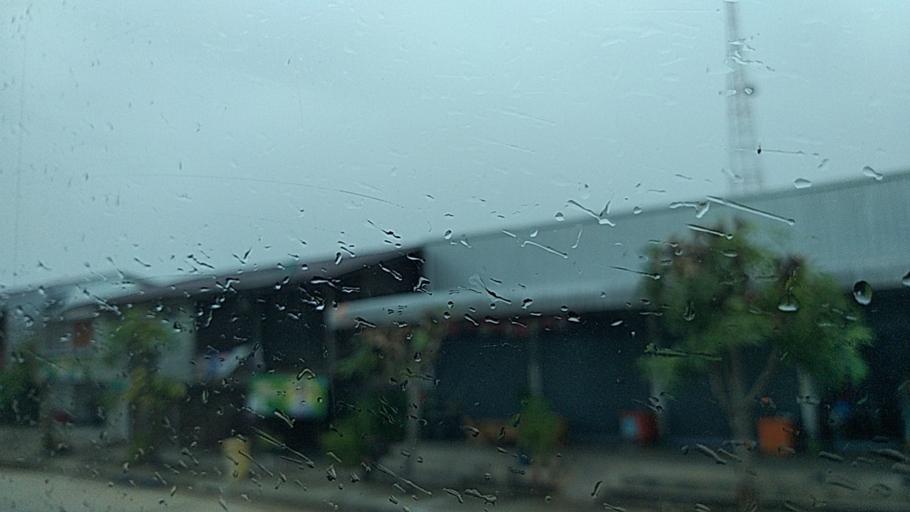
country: TH
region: Maha Sarakham
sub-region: Amphoe Borabue
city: Borabue
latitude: 16.0381
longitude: 103.1225
